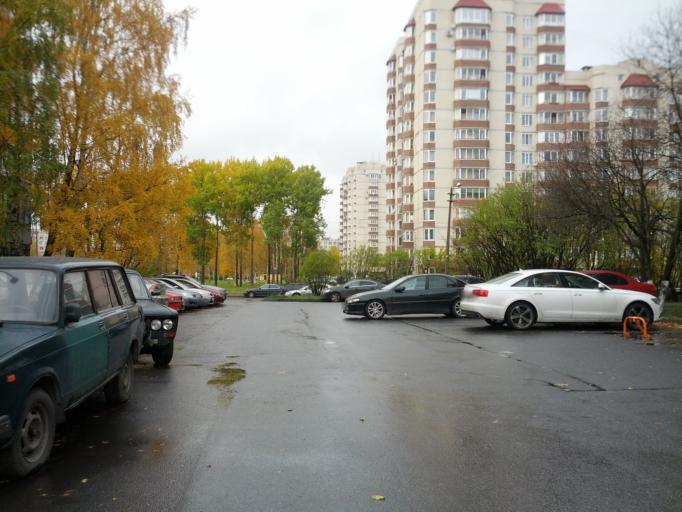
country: RU
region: St.-Petersburg
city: Krasnogvargeisky
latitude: 59.9084
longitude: 30.4709
